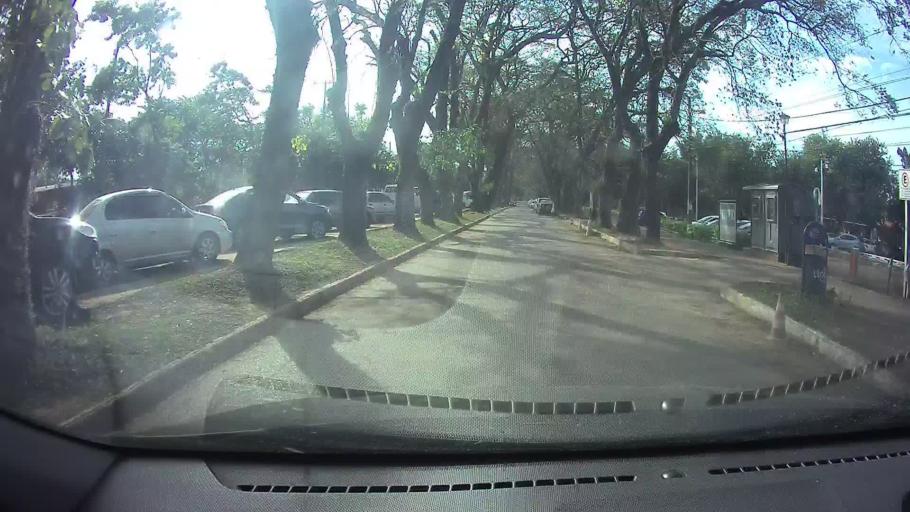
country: PY
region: Central
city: Fernando de la Mora
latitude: -25.3353
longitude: -57.5227
